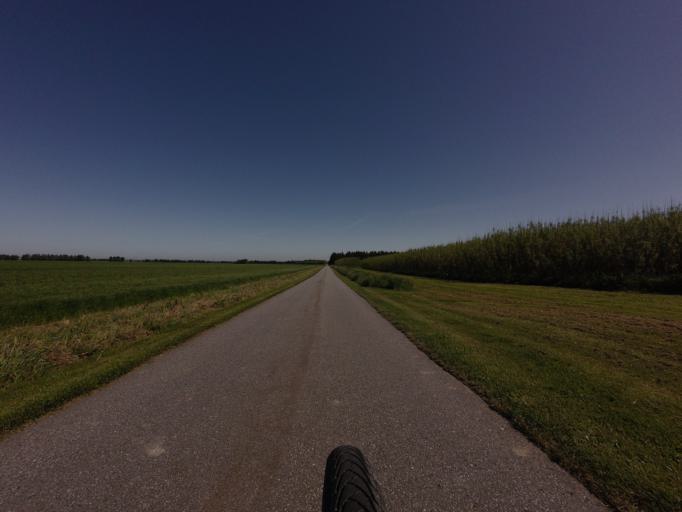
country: DK
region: North Denmark
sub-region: Hjorring Kommune
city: Vra
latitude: 57.3722
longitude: 9.8117
